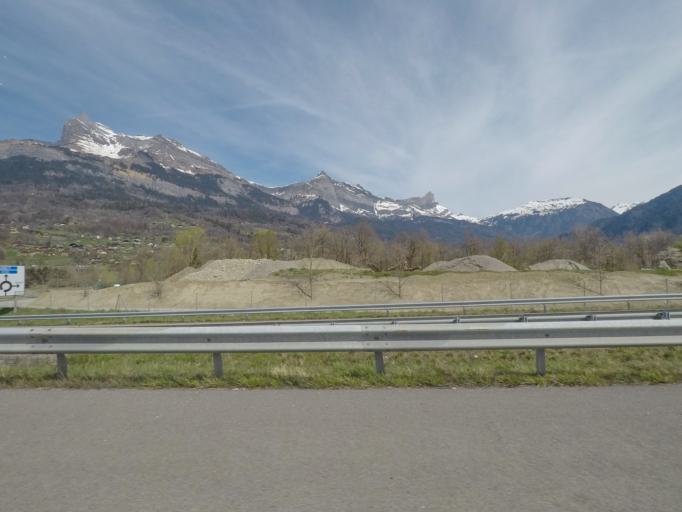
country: FR
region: Rhone-Alpes
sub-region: Departement de la Haute-Savoie
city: Passy
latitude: 45.9122
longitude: 6.6922
